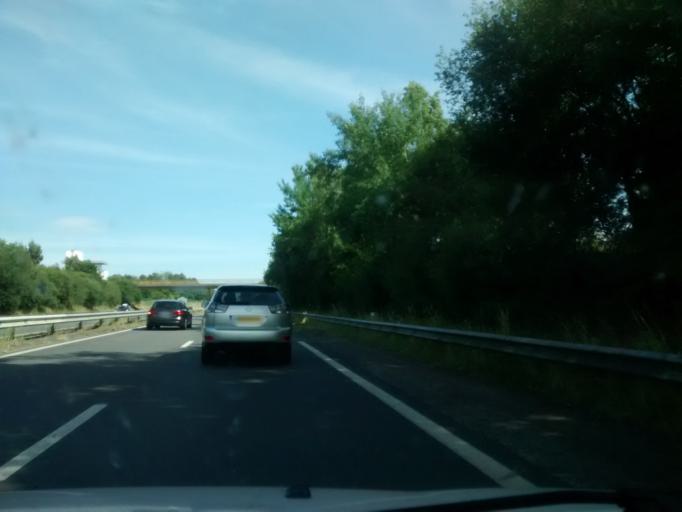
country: FR
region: Brittany
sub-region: Departement des Cotes-d'Armor
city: Plenee-Jugon
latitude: 48.3997
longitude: -2.4079
